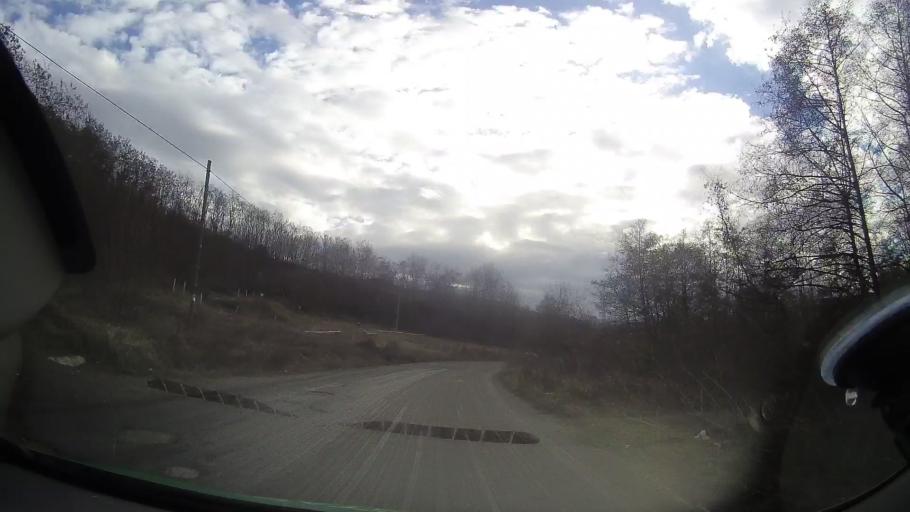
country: RO
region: Cluj
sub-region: Comuna Baisoara
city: Baisoara
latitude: 46.5840
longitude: 23.4621
